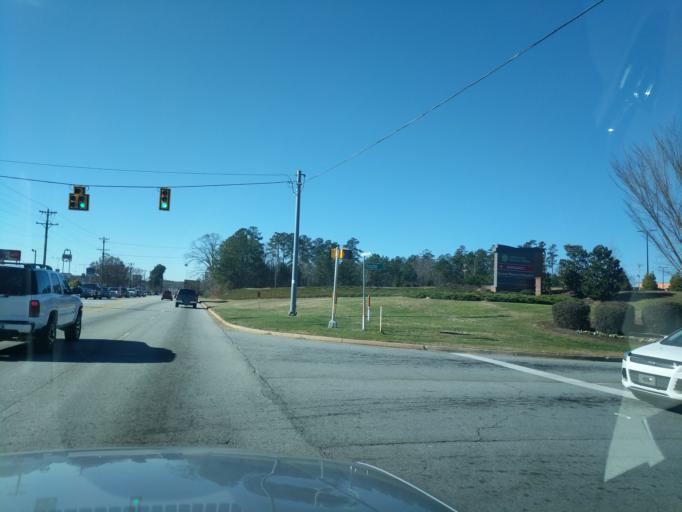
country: US
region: South Carolina
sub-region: Oconee County
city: Seneca
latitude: 34.6926
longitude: -82.9854
